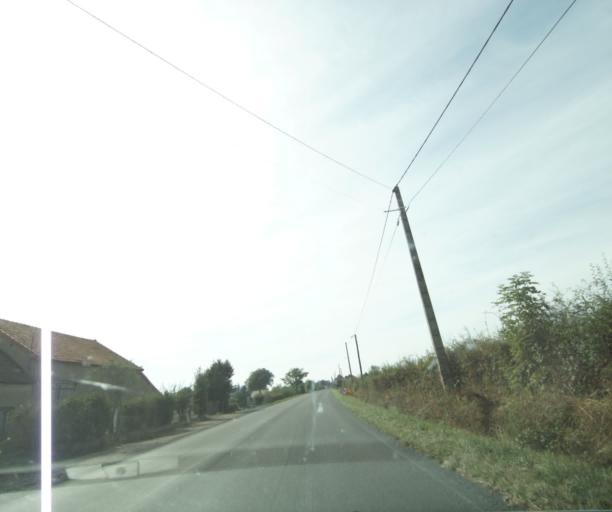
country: FR
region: Auvergne
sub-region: Departement de l'Allier
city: Saint-Francois
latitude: 46.4196
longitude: 3.9066
